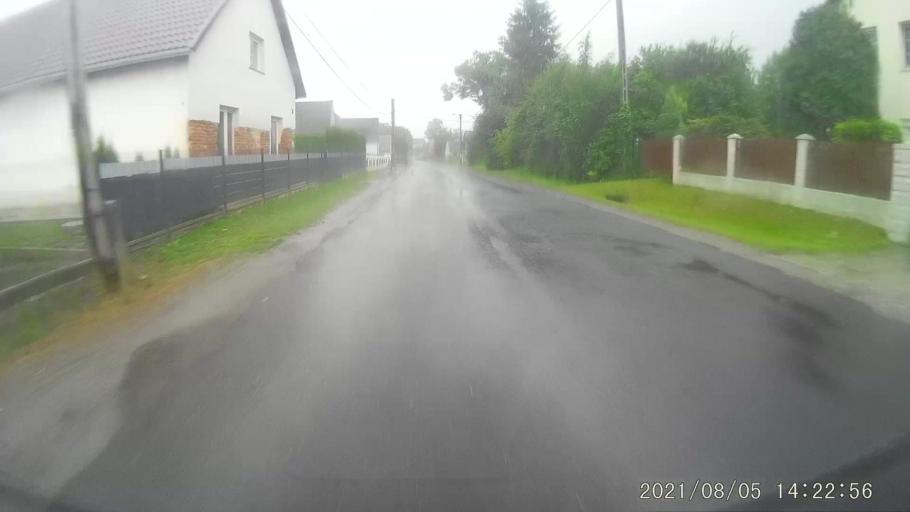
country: PL
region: Opole Voivodeship
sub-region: Powiat nyski
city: Korfantow
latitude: 50.4793
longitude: 17.6518
